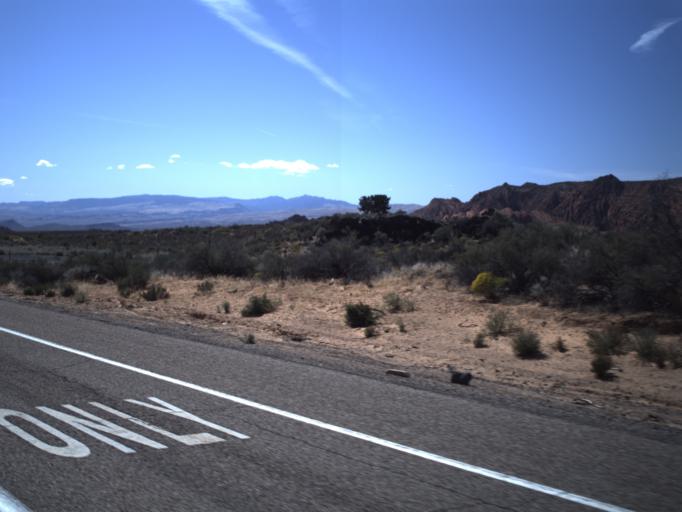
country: US
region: Utah
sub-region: Washington County
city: Ivins
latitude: 37.2316
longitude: -113.6339
